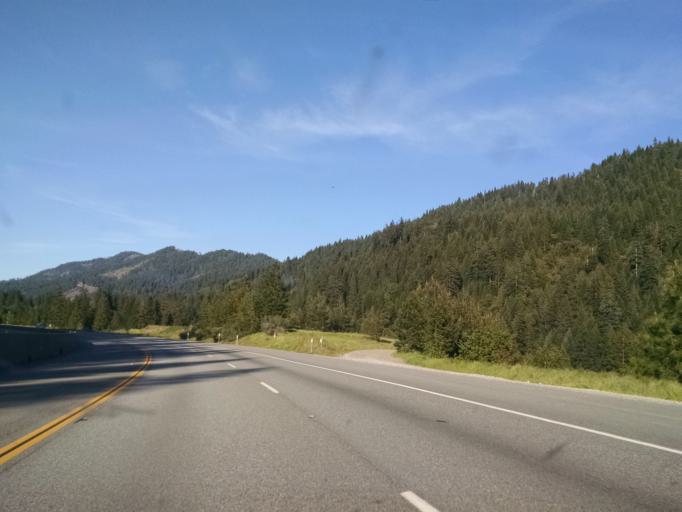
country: US
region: California
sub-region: Siskiyou County
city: Dunsmuir
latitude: 41.0488
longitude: -122.3826
